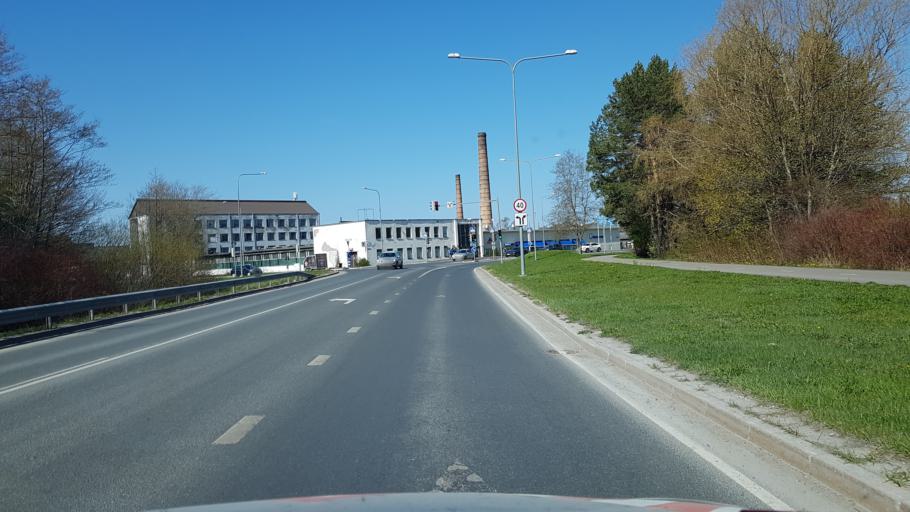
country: EE
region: Harju
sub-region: Viimsi vald
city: Haabneeme
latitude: 59.5066
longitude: 24.8237
